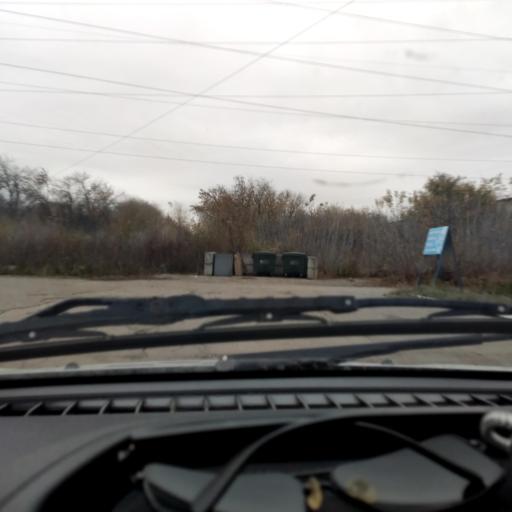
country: RU
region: Samara
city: Tol'yatti
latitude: 53.5392
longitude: 49.4420
